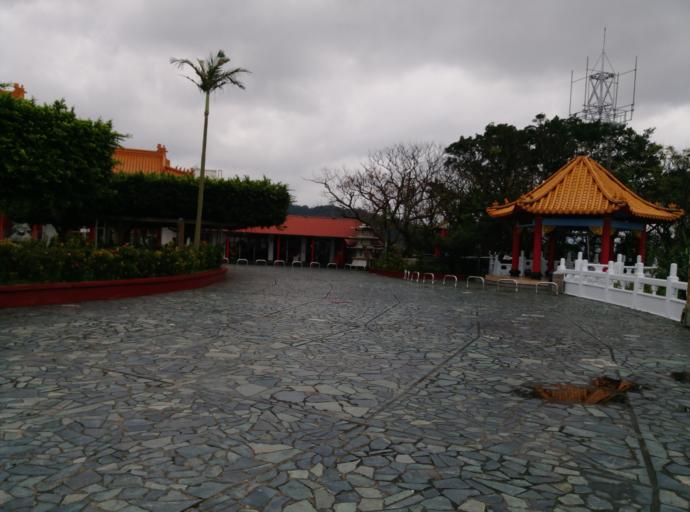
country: TW
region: Taiwan
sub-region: Keelung
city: Keelung
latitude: 25.1336
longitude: 121.7503
